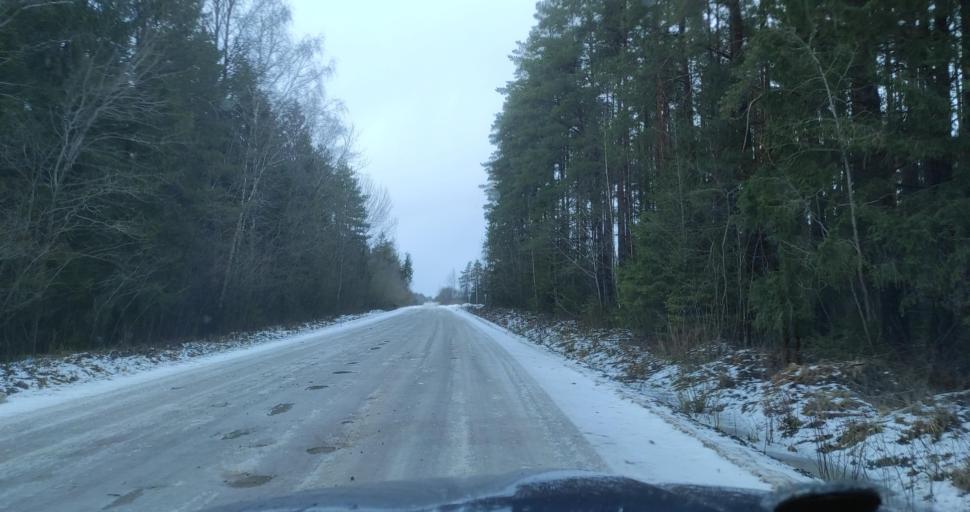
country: LV
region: Dundaga
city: Dundaga
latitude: 57.4924
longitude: 22.0201
